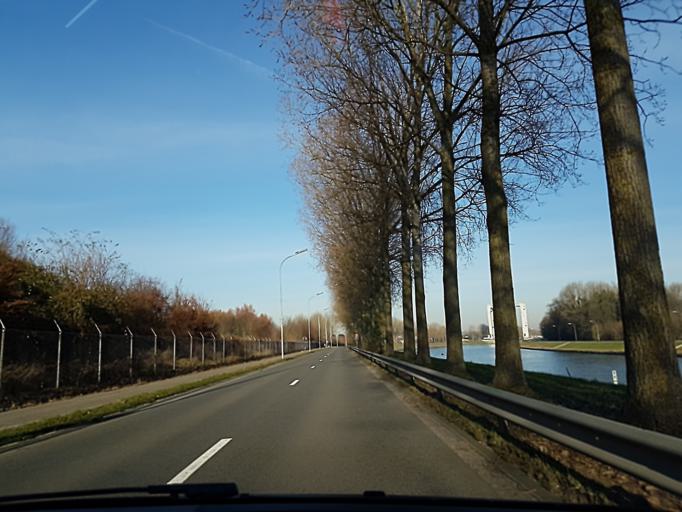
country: BE
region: Flanders
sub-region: Provincie Vlaams-Brabant
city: Kapelle-op-den-Bos
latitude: 51.0271
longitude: 4.3575
